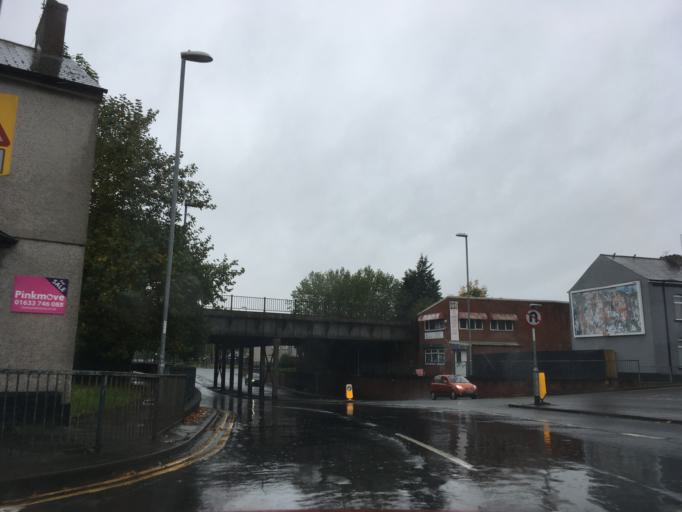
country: GB
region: Wales
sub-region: Newport
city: Newport
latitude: 51.5889
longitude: -2.9782
